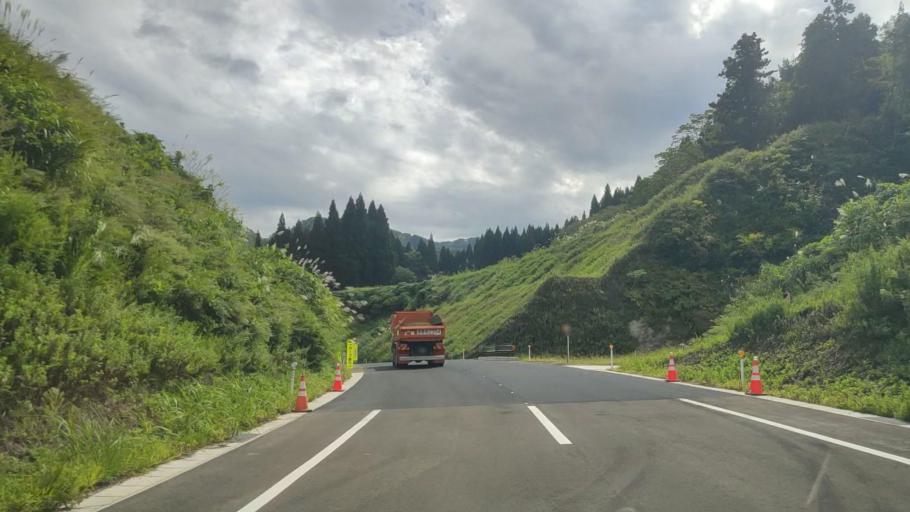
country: JP
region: Niigata
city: Arai
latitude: 36.9475
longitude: 138.2853
